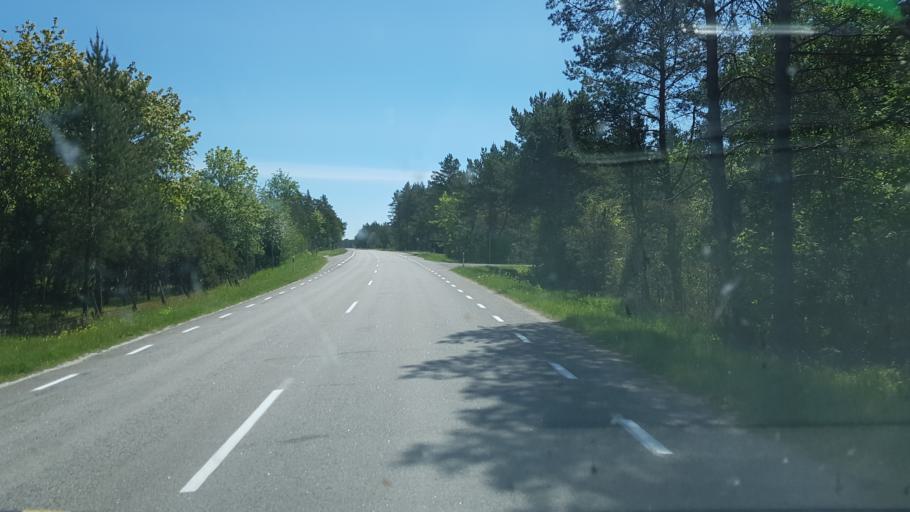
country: EE
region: Saare
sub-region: Kuressaare linn
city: Kuressaare
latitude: 58.3012
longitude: 22.2567
